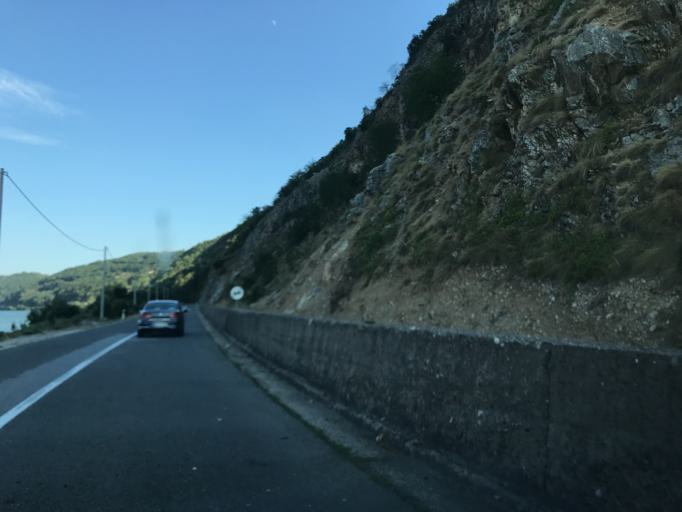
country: RO
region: Mehedinti
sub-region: Comuna Svinita
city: Svinita
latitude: 44.4830
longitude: 22.0899
